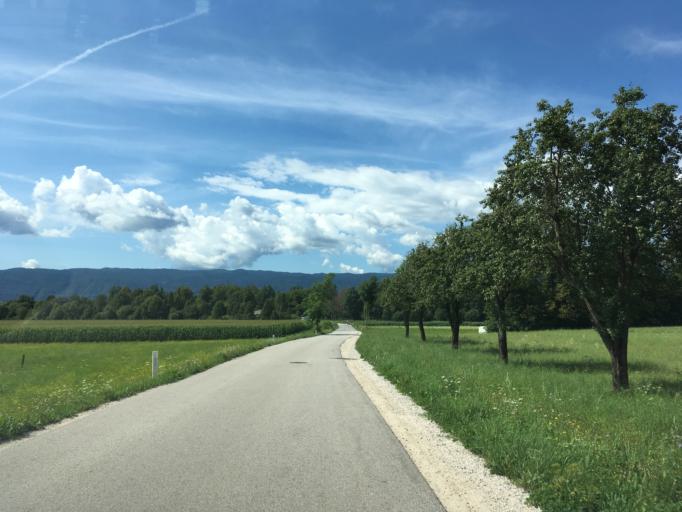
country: SI
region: Radovljica
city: Lesce
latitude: 46.3804
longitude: 14.1734
